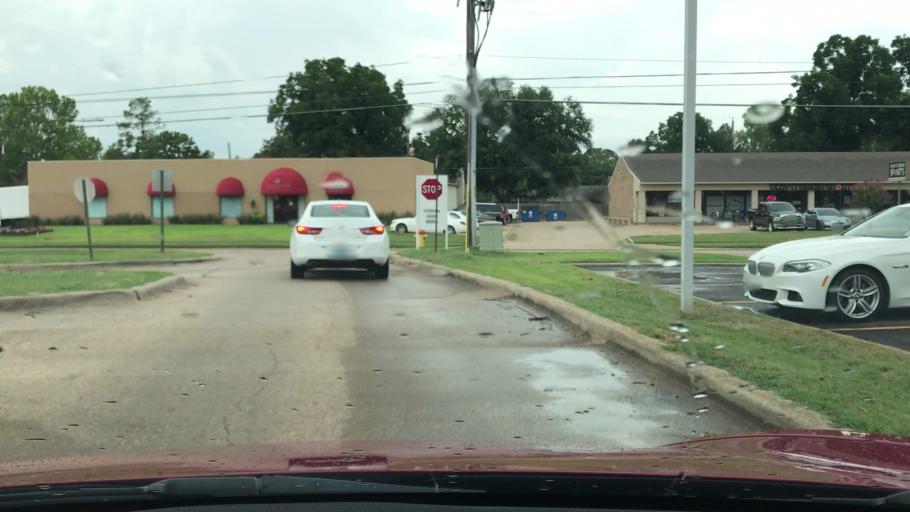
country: US
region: Louisiana
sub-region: Bossier Parish
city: Bossier City
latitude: 32.4433
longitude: -93.7097
